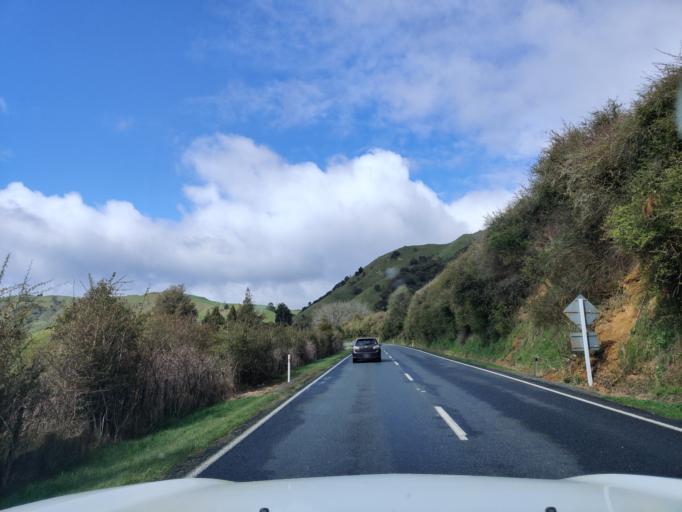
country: NZ
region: Waikato
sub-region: Otorohanga District
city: Otorohanga
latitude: -38.5893
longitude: 175.2176
